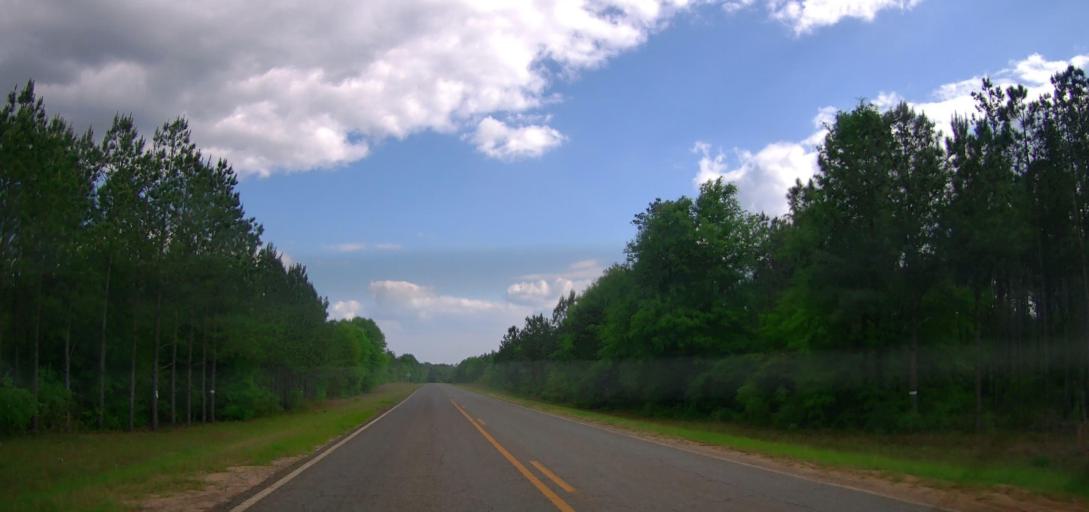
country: US
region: Georgia
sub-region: Johnson County
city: Wrightsville
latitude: 32.7479
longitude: -82.9250
